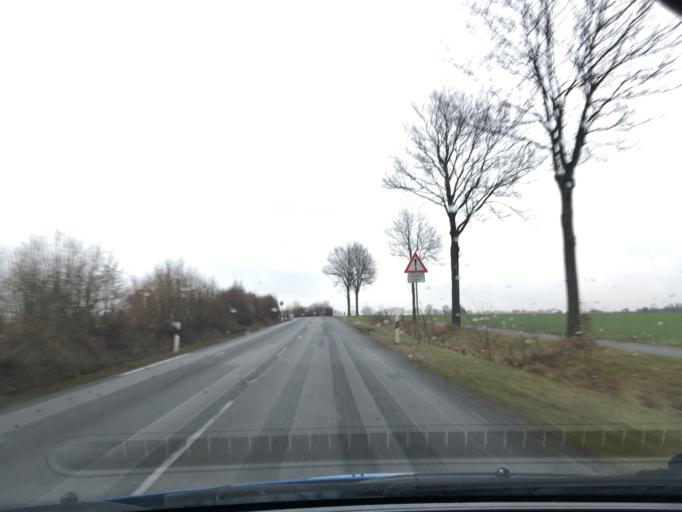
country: DE
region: Schleswig-Holstein
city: Breitenfelde
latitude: 53.5946
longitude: 10.6425
